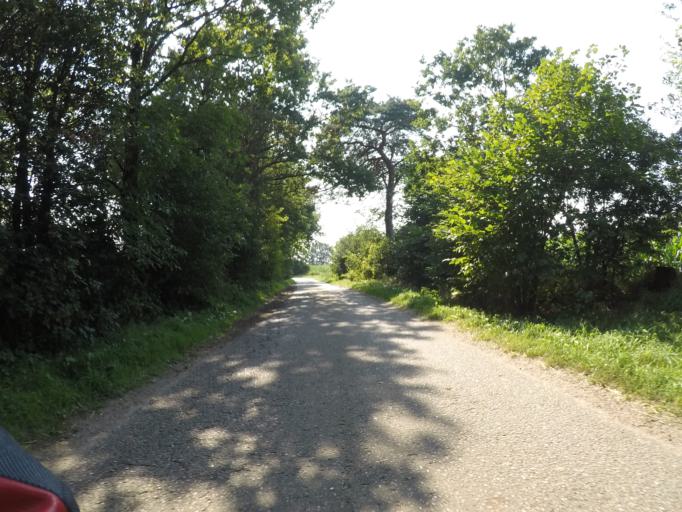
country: DE
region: Schleswig-Holstein
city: Stuvenborn
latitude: 53.8603
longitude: 10.1503
